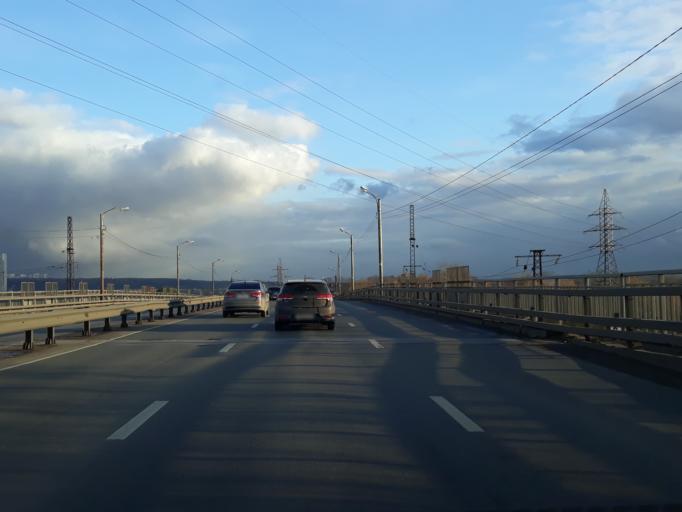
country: RU
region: Nizjnij Novgorod
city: Nizhniy Novgorod
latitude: 56.3067
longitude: 43.9045
